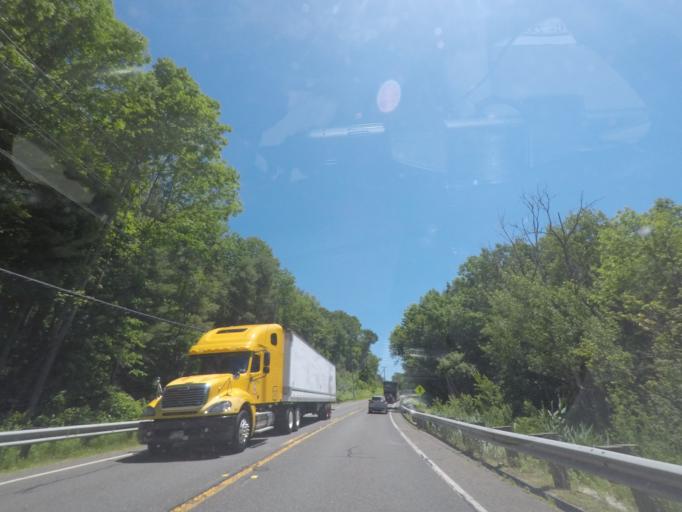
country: US
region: Massachusetts
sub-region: Berkshire County
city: Becket
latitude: 42.2917
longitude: -73.1579
